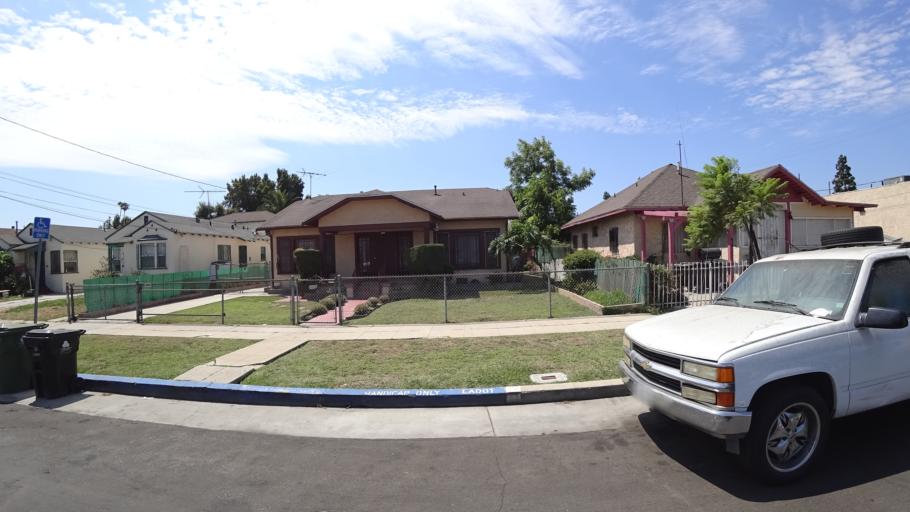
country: US
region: California
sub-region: Los Angeles County
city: Westmont
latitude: 33.9510
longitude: -118.2910
